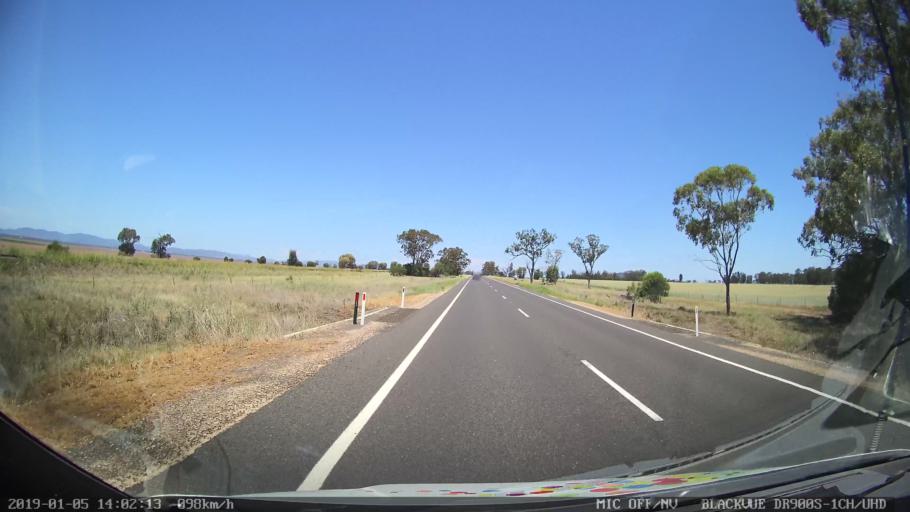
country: AU
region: New South Wales
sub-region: Gunnedah
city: Gunnedah
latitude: -31.1775
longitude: 150.3350
